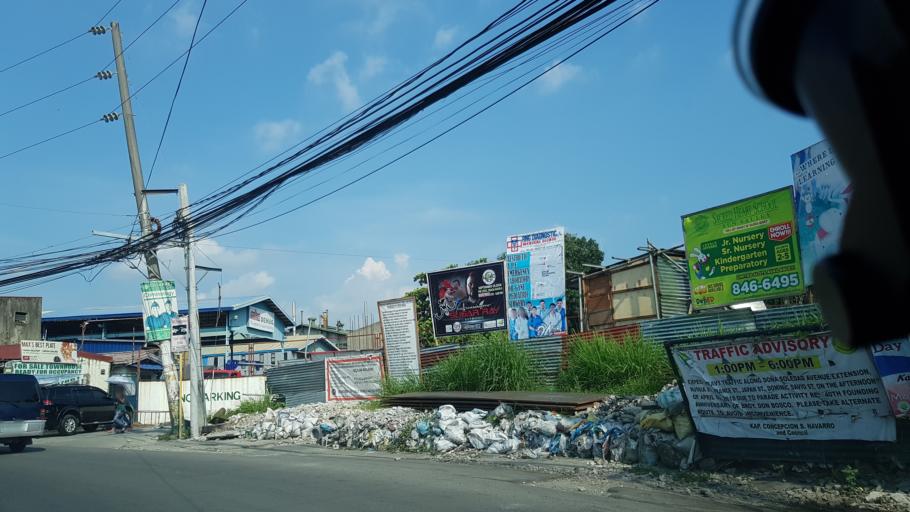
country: PH
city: Sambayanihan People's Village
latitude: 14.4824
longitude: 121.0370
